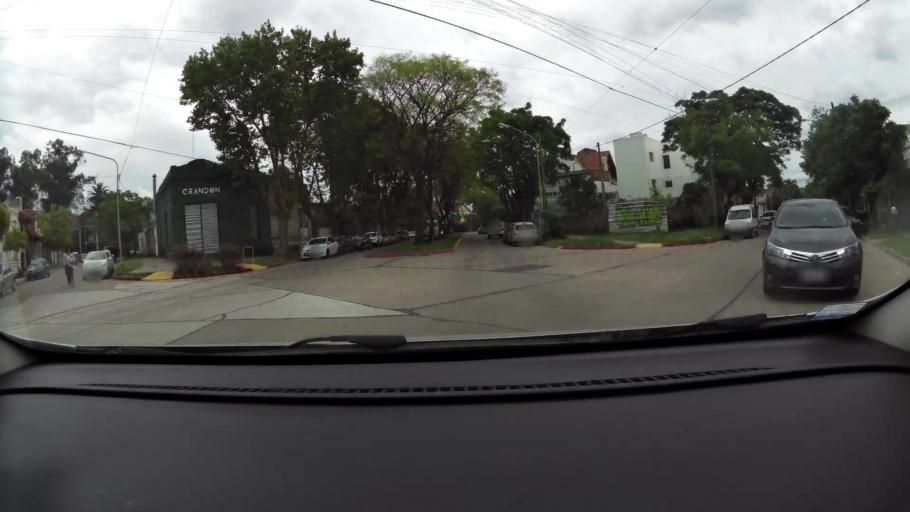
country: AR
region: Buenos Aires
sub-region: Partido de Campana
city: Campana
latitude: -34.1591
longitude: -58.9634
